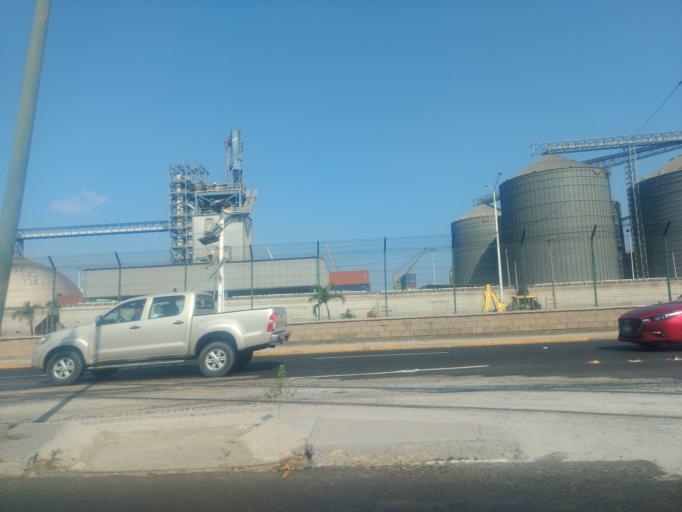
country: MX
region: Colima
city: Tapeixtles
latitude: 19.0633
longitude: -104.2897
